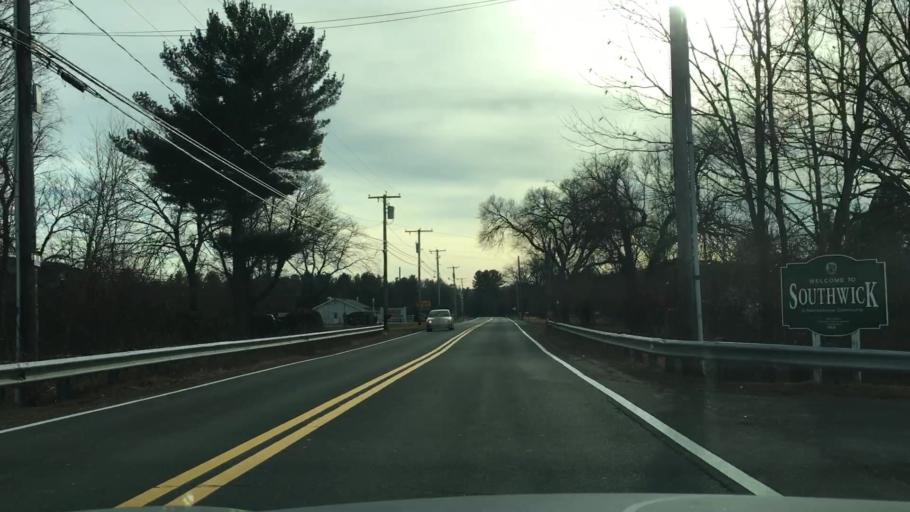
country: US
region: Massachusetts
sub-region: Hampden County
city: Southwick
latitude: 42.0868
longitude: -72.7648
